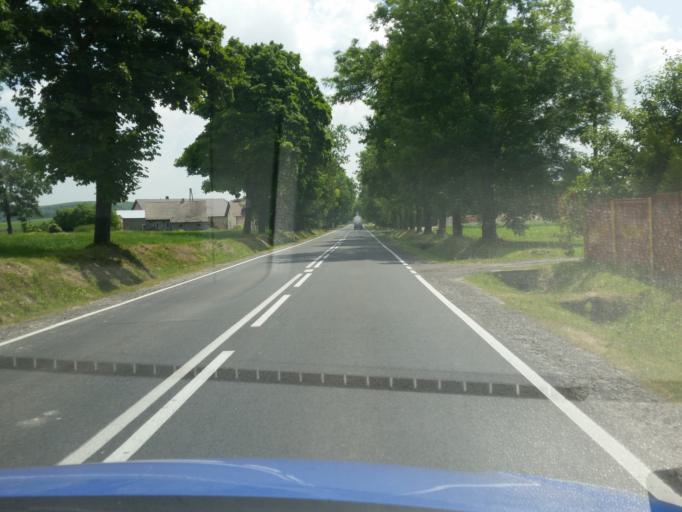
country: PL
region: Lesser Poland Voivodeship
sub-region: Powiat miechowski
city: Miechow
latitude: 50.3579
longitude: 20.0882
